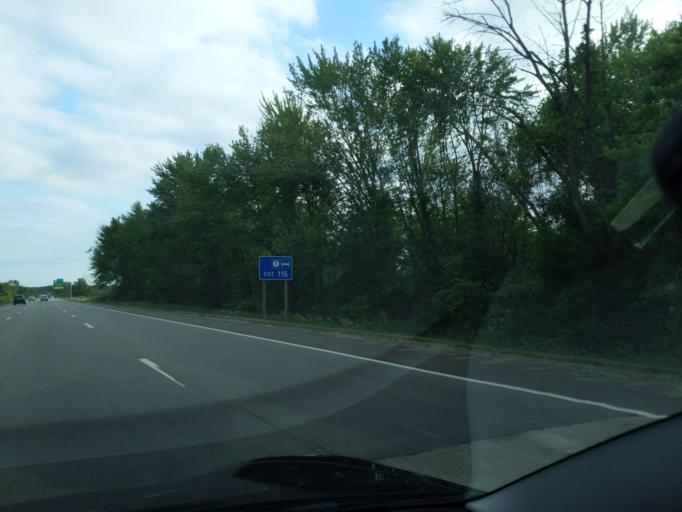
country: US
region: Michigan
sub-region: Muskegon County
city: Muskegon
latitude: 43.2715
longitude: -86.2041
